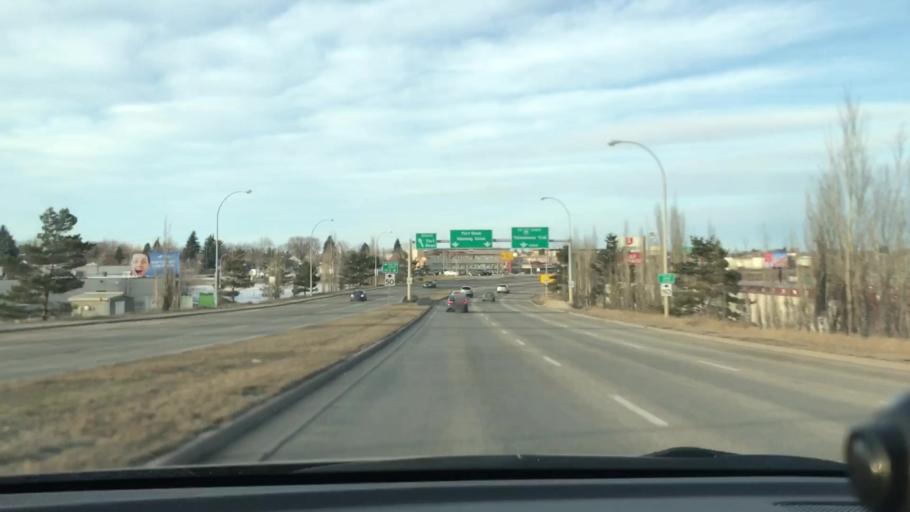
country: CA
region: Alberta
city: Edmonton
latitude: 53.5771
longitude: -113.4537
